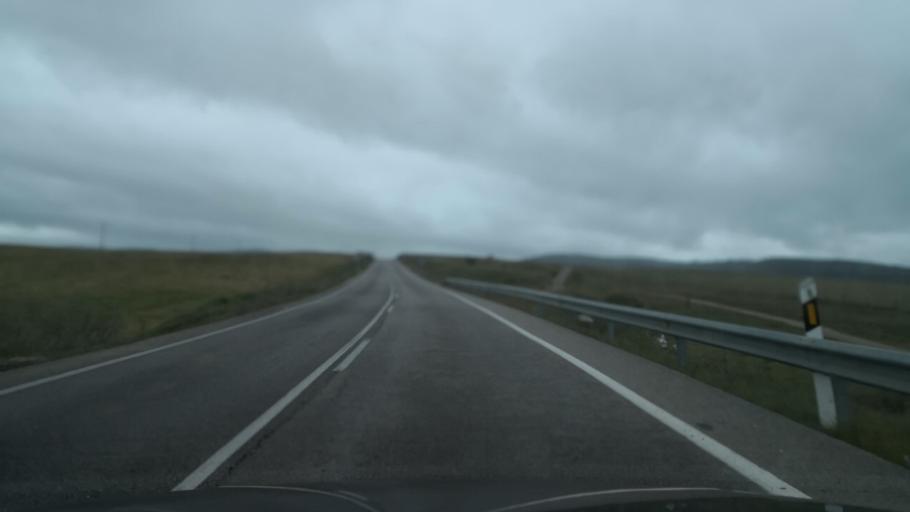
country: ES
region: Extremadura
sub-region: Provincia de Caceres
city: Casar de Caceres
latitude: 39.5178
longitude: -6.3977
